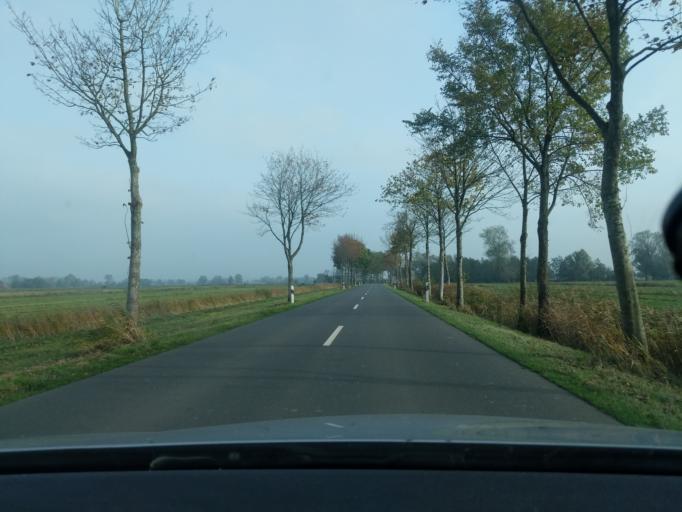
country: DE
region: Lower Saxony
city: Ihlienworth
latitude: 53.7224
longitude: 8.9416
